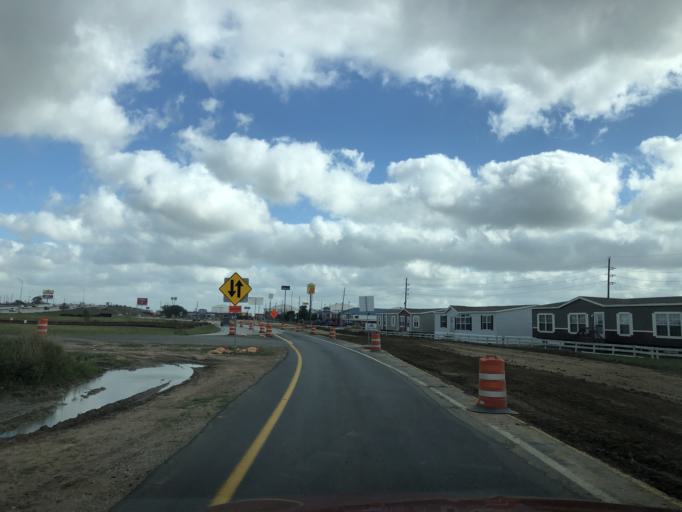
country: US
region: Texas
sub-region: Austin County
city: Sealy
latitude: 29.7620
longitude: -96.1577
